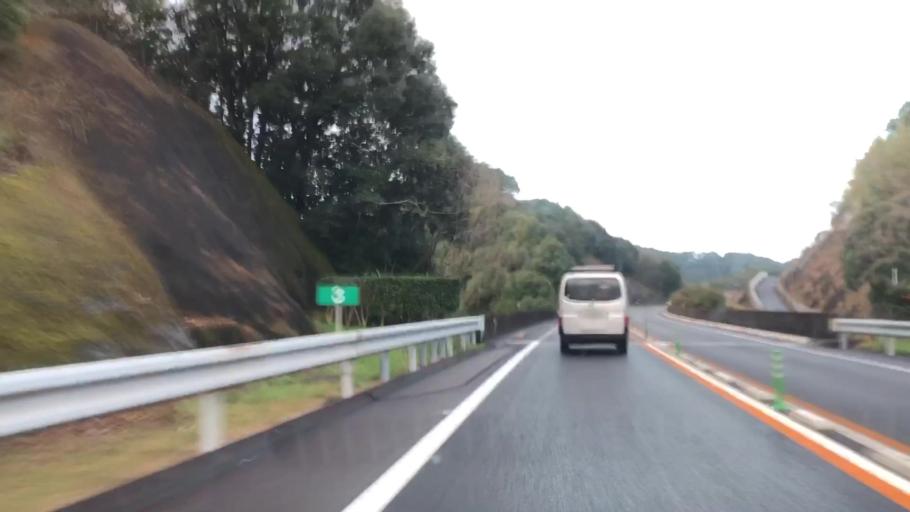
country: JP
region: Saga Prefecture
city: Ureshinomachi-shimojuku
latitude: 33.1431
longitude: 129.9577
